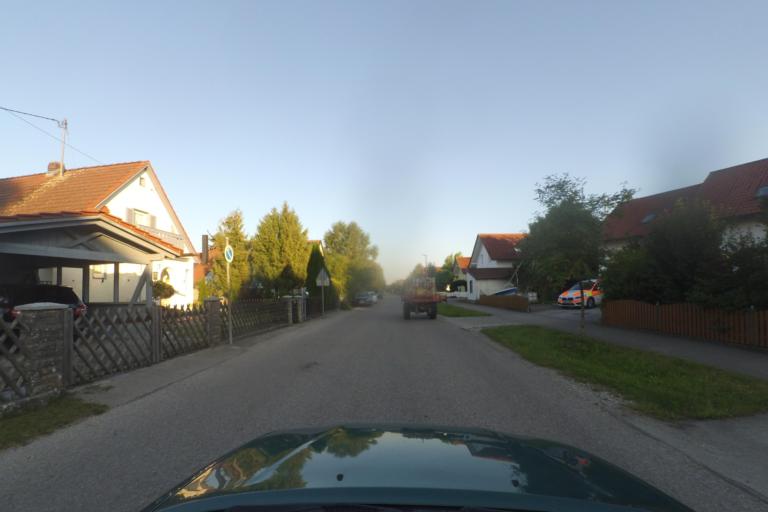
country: DE
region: Bavaria
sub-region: Upper Bavaria
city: Weil
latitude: 48.0981
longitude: 10.9106
